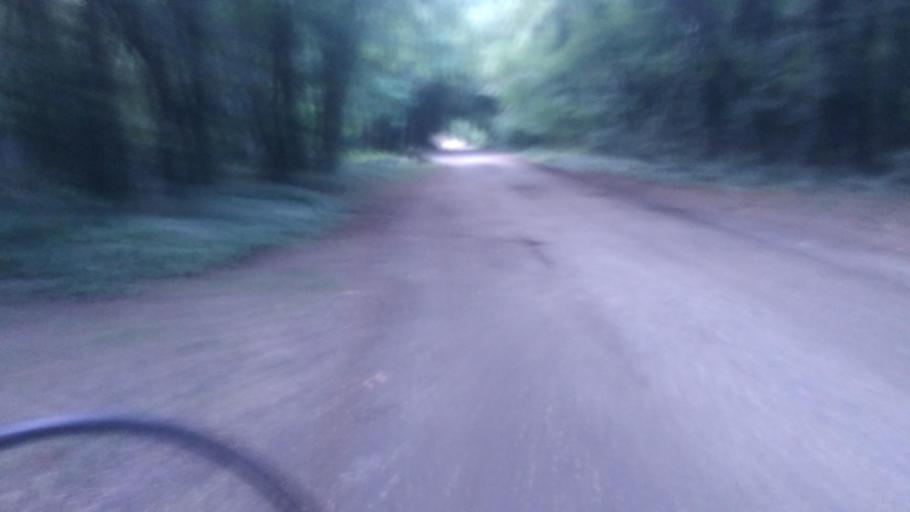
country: HU
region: Budapest
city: Budapest XVIII. keruelet
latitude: 47.4740
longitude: 19.1950
